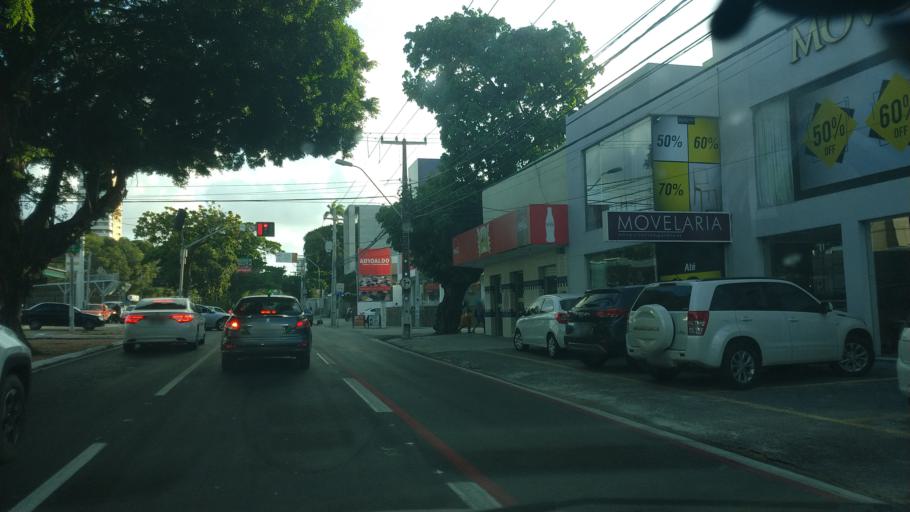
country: BR
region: Rio Grande do Norte
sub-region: Natal
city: Natal
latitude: -5.7908
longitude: -35.1971
